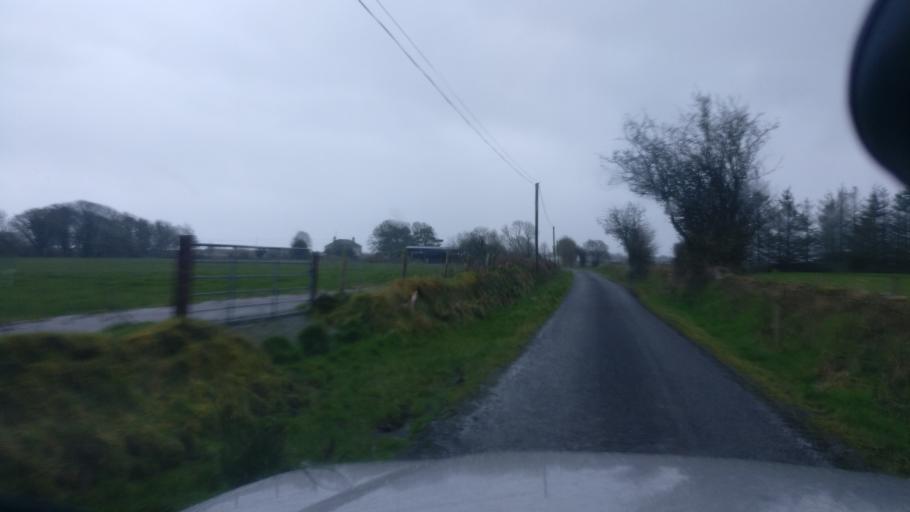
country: IE
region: Connaught
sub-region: County Galway
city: Loughrea
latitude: 53.2352
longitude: -8.4218
